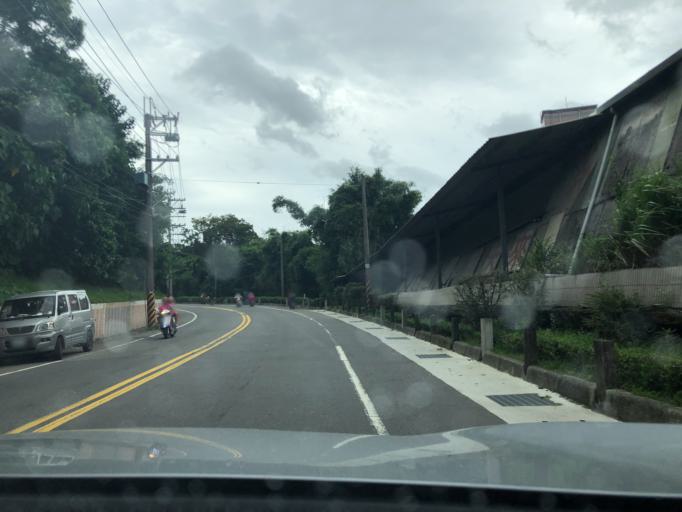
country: TW
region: Taiwan
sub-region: Taoyuan
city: Taoyuan
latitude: 24.9436
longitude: 121.3398
